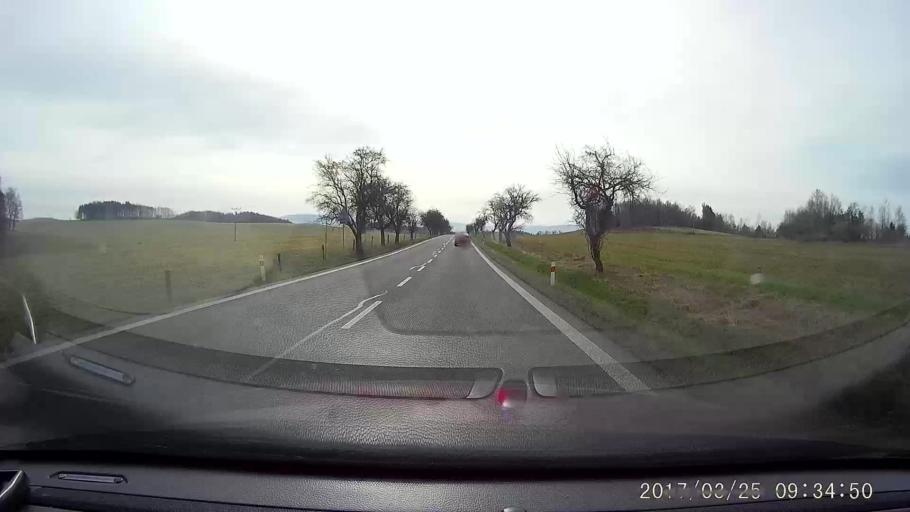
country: CZ
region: Liberecky
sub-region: Okres Liberec
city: Frydlant
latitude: 50.9699
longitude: 15.0932
